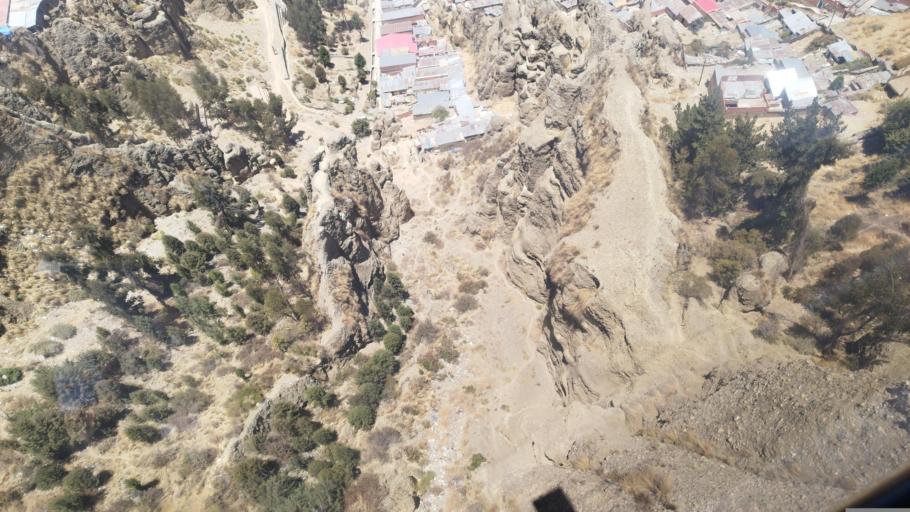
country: BO
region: La Paz
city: La Paz
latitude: -16.5033
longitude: -68.1609
